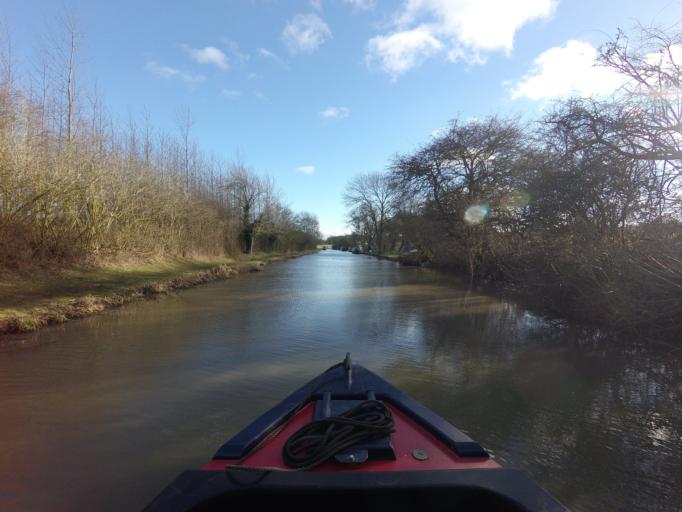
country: GB
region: England
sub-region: Northamptonshire
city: Blisworth
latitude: 52.1946
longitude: -0.9669
